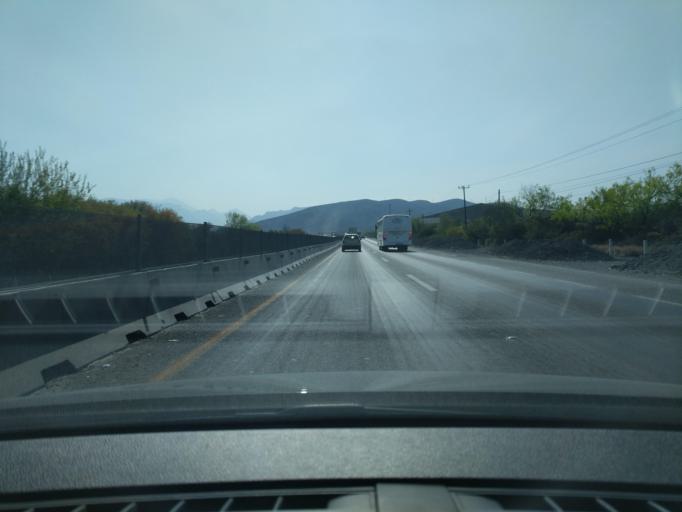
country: MX
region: Nuevo Leon
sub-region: Garcia
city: Los Parques
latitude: 25.7703
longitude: -100.4772
